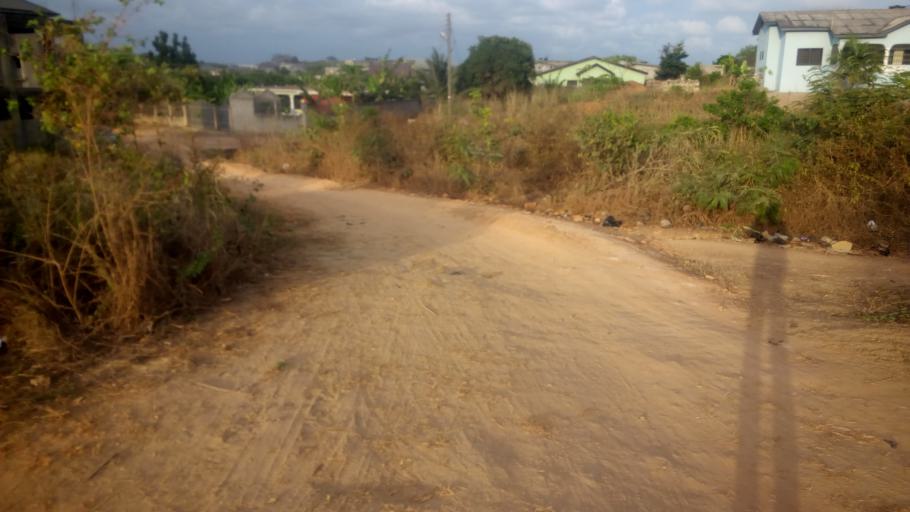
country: GH
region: Central
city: Elmina
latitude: 5.1189
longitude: -1.3037
